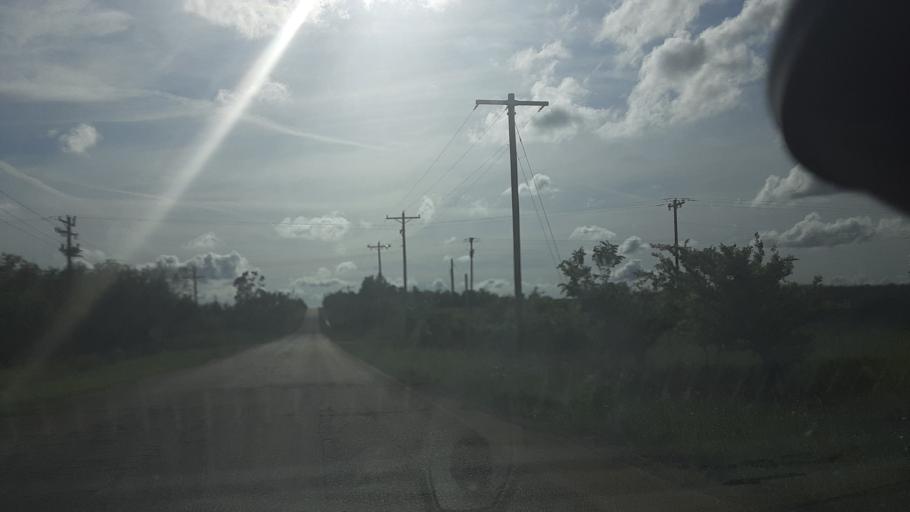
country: US
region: Oklahoma
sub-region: Logan County
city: Langston
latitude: 36.0578
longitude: -97.3891
